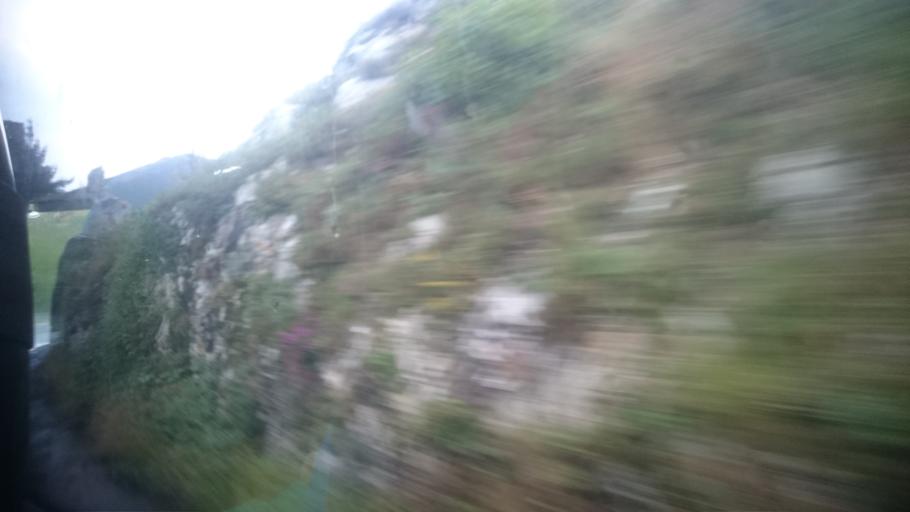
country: ES
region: Asturias
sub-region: Province of Asturias
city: Cangas de Onis
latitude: 43.3289
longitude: -5.0811
